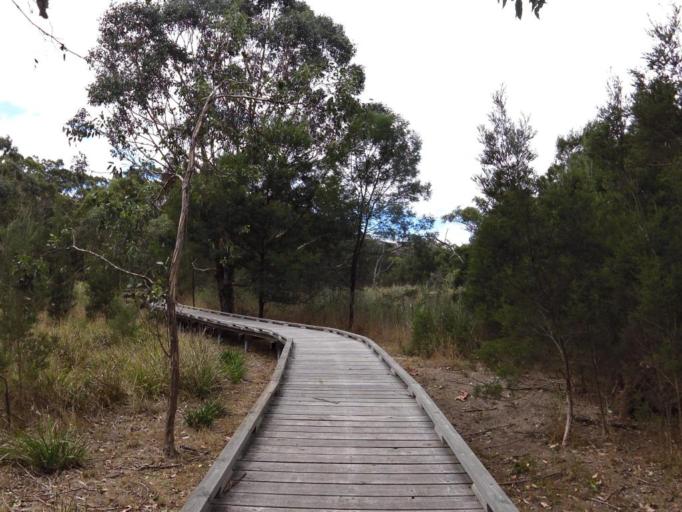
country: AU
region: Victoria
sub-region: Mornington Peninsula
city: Mount Martha
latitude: -38.2680
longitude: 145.0474
